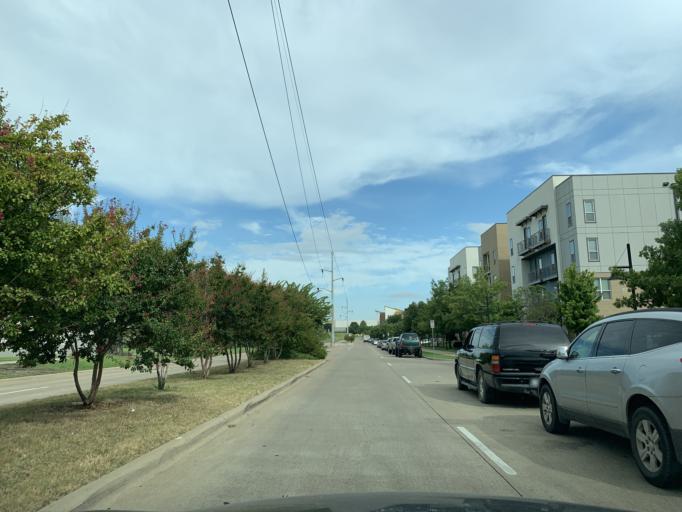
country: US
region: Texas
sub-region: Dallas County
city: Cockrell Hill
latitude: 32.7553
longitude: -96.8767
